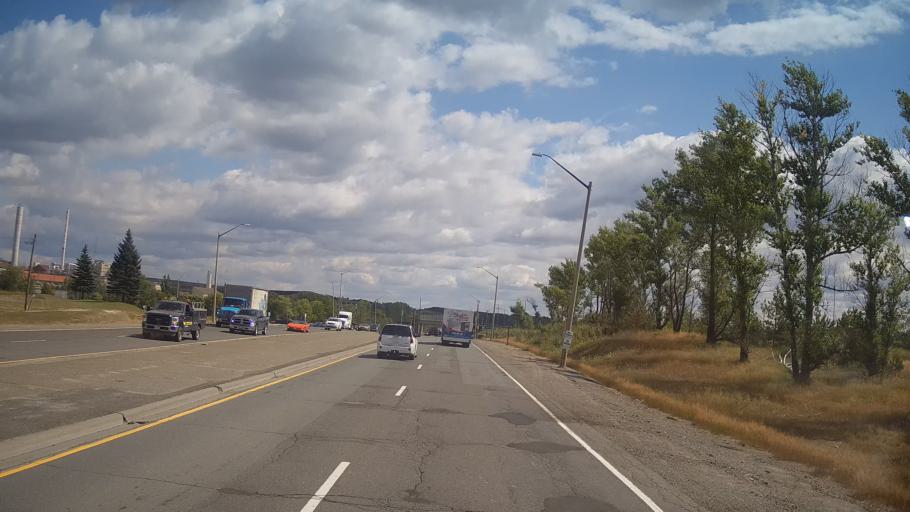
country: CA
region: Ontario
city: Greater Sudbury
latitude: 46.4677
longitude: -81.0623
